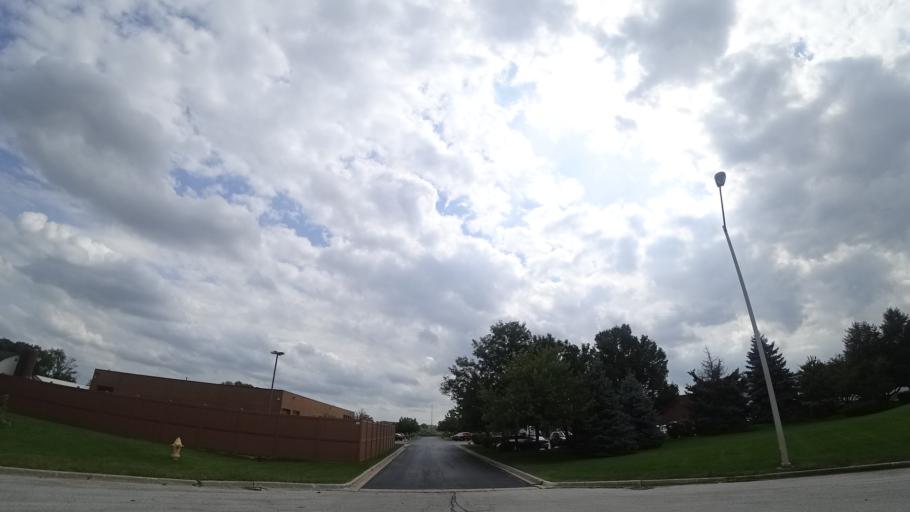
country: US
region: Illinois
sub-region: Cook County
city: Tinley Park
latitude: 41.5526
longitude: -87.8057
